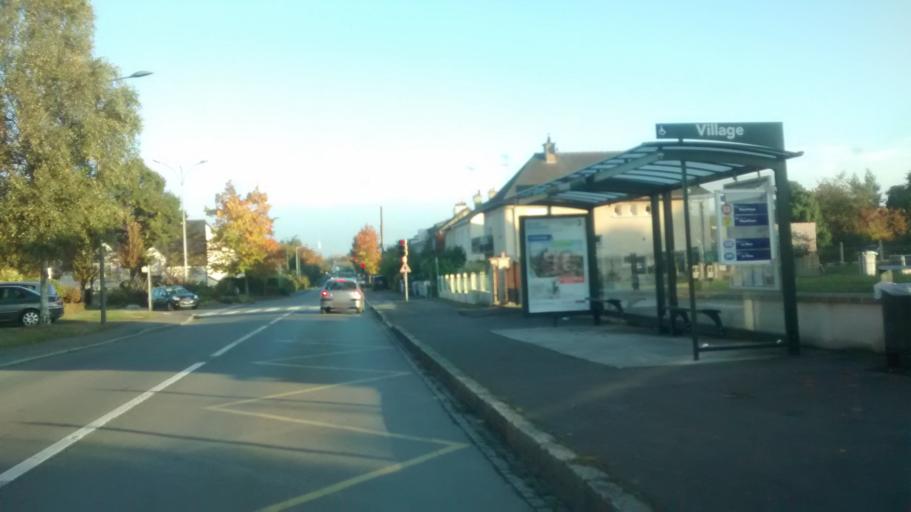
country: FR
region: Brittany
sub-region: Departement d'Ille-et-Vilaine
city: Le Rheu
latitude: 48.1247
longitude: -1.8117
